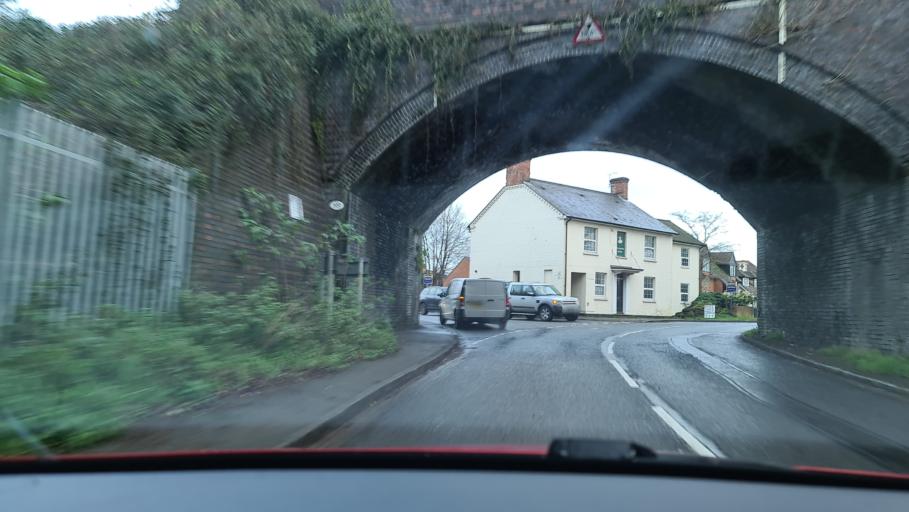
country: GB
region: England
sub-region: Buckinghamshire
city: Princes Risborough
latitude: 51.7320
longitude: -0.8551
